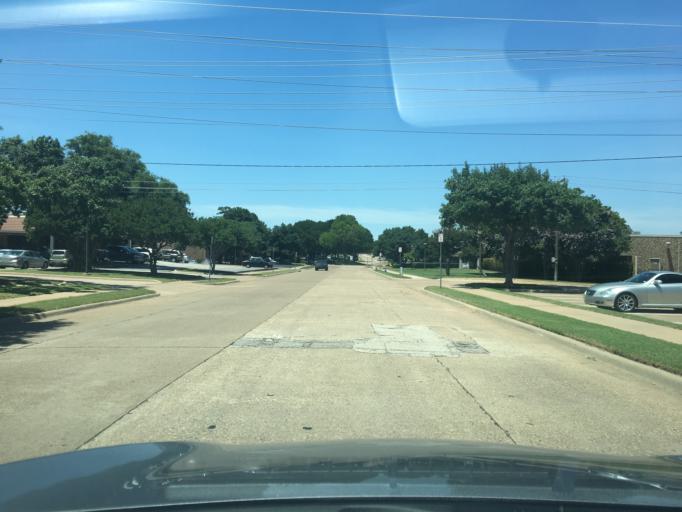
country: US
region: Texas
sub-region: Dallas County
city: Richardson
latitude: 32.9564
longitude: -96.7033
